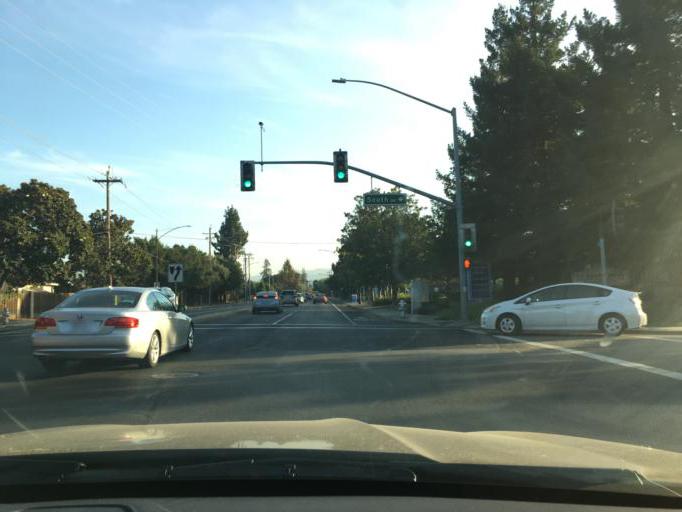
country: US
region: California
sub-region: Santa Clara County
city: Mountain View
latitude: 37.3675
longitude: -122.0780
